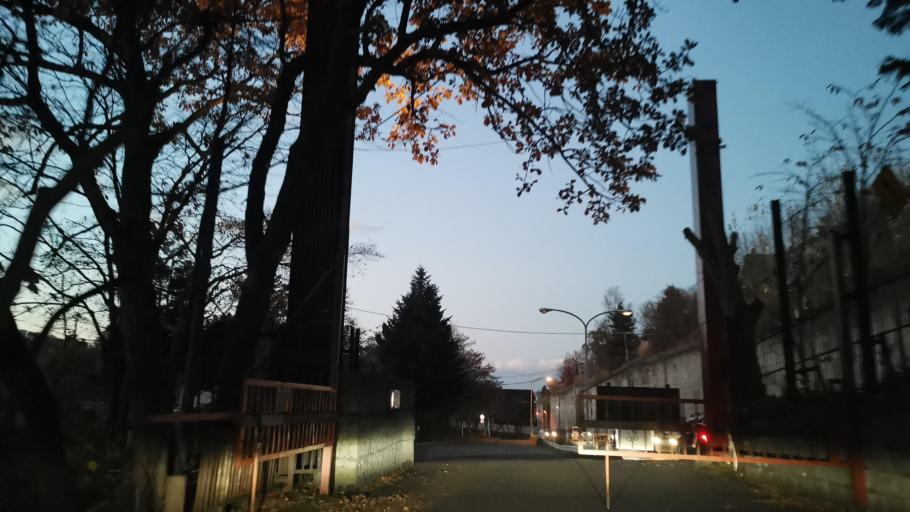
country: JP
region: Hokkaido
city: Sapporo
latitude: 42.9931
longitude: 141.3659
